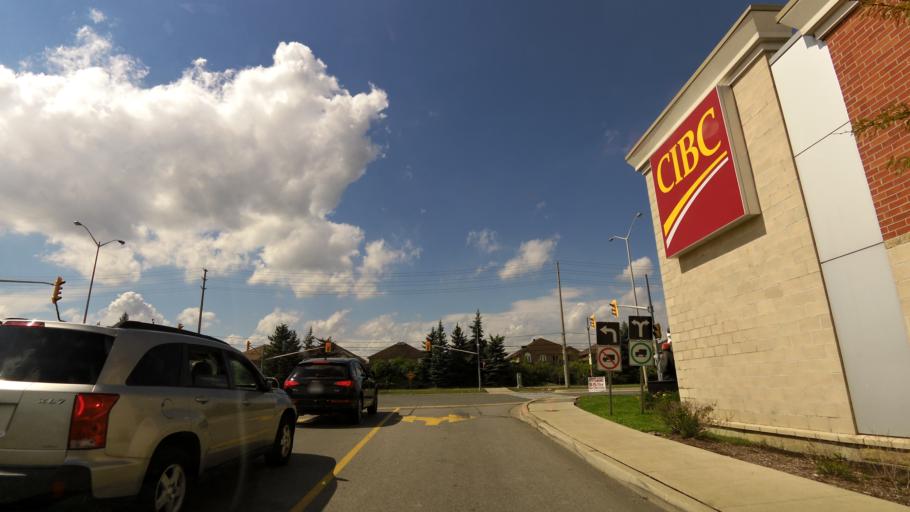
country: CA
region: Ontario
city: Brampton
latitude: 43.7610
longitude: -79.7244
